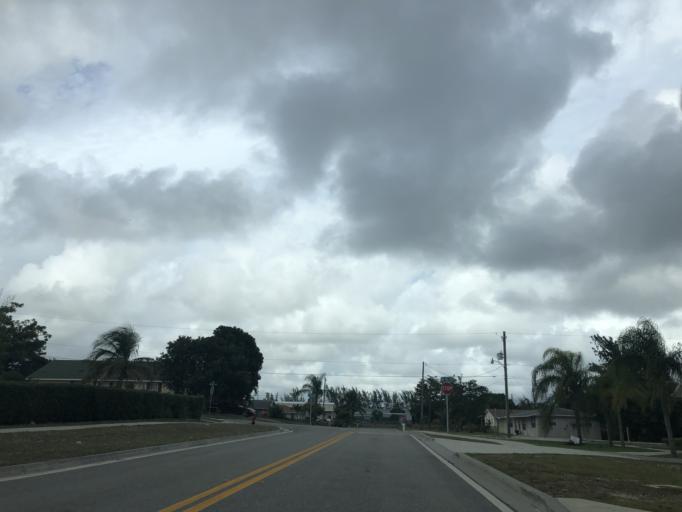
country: US
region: Florida
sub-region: Palm Beach County
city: Riviera Beach
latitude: 26.7697
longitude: -80.0651
